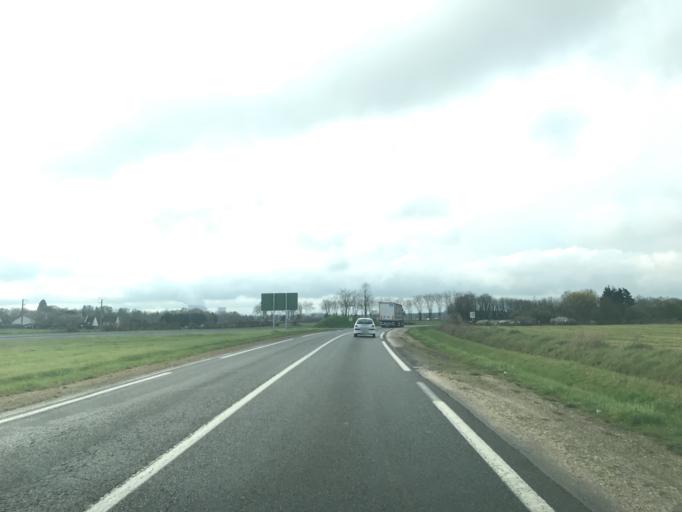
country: FR
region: Centre
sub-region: Departement du Loiret
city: Nevoy
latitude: 47.7149
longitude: 2.5880
